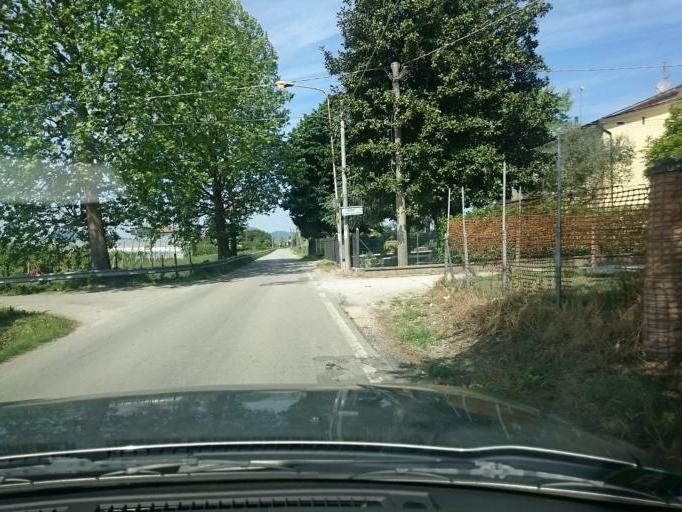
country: IT
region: Veneto
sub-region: Provincia di Padova
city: San Pietro Viminario
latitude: 45.2547
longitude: 11.8355
